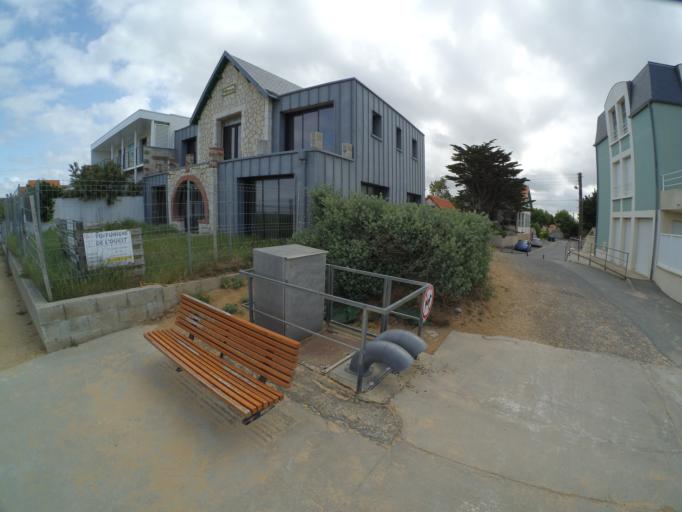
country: FR
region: Poitou-Charentes
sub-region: Departement de la Charente-Maritime
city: Chatelaillon-Plage
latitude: 46.0658
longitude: -1.0929
